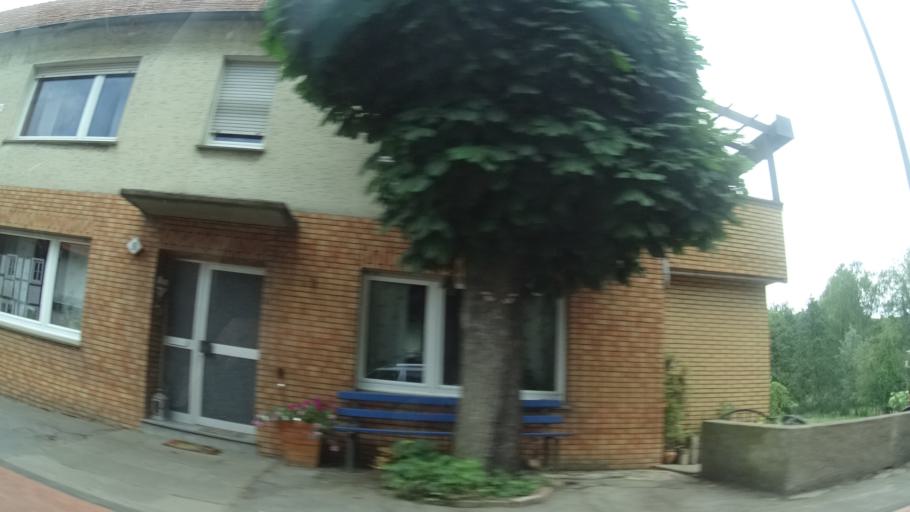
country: DE
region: North Rhine-Westphalia
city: Brakel
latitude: 51.6600
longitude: 9.1482
